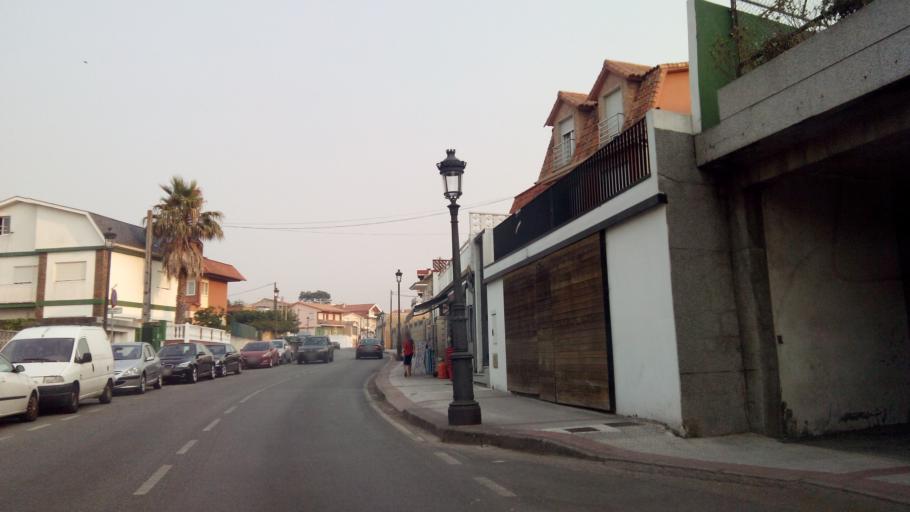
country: ES
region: Galicia
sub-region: Provincia de Pontevedra
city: Nigran
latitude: 42.1524
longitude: -8.8266
